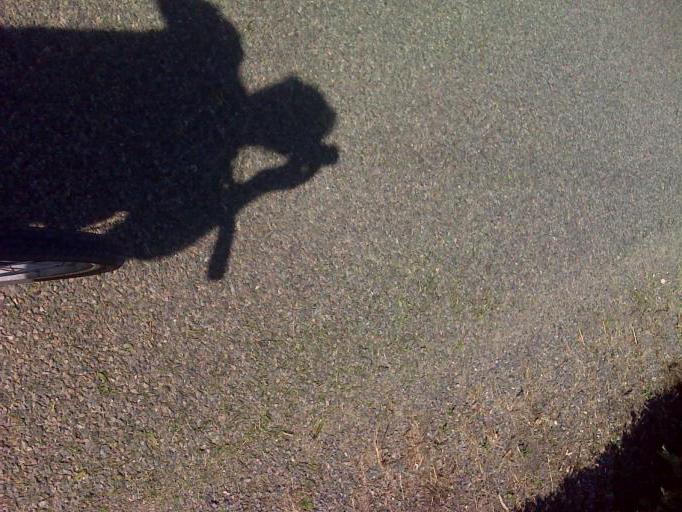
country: FR
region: Auvergne
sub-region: Departement de l'Allier
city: Ebreuil
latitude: 46.1098
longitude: 3.0766
